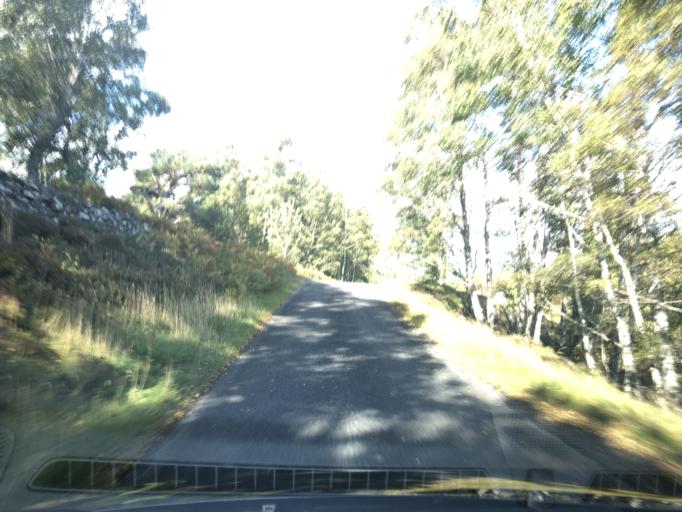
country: GB
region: Scotland
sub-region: Highland
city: Aviemore
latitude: 57.0818
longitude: -3.9005
